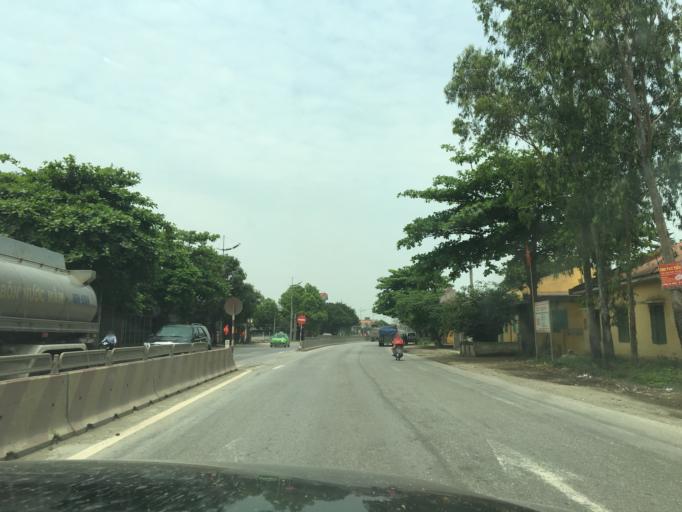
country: VN
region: Ninh Binh
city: Thi Tran Tam Diep
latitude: 20.1695
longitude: 105.9411
